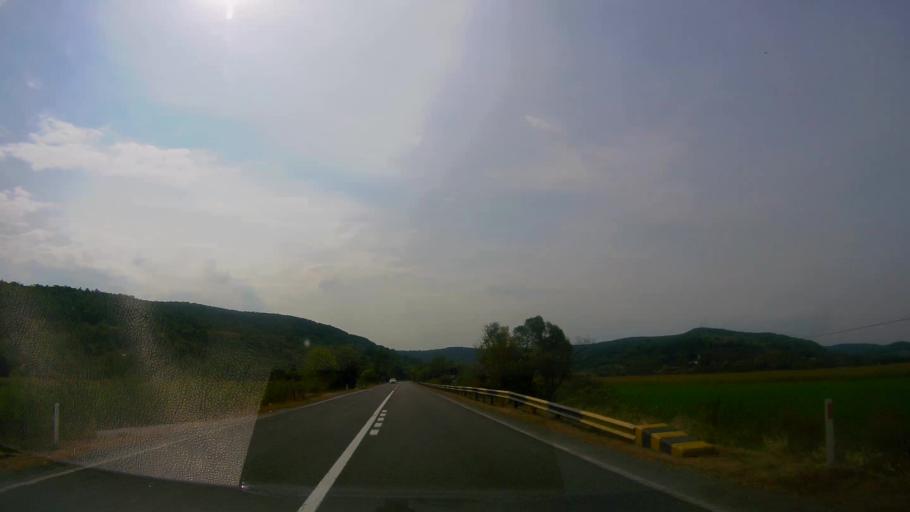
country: RO
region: Salaj
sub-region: Comuna Zimbor
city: Zimbor
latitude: 46.9925
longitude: 23.2503
